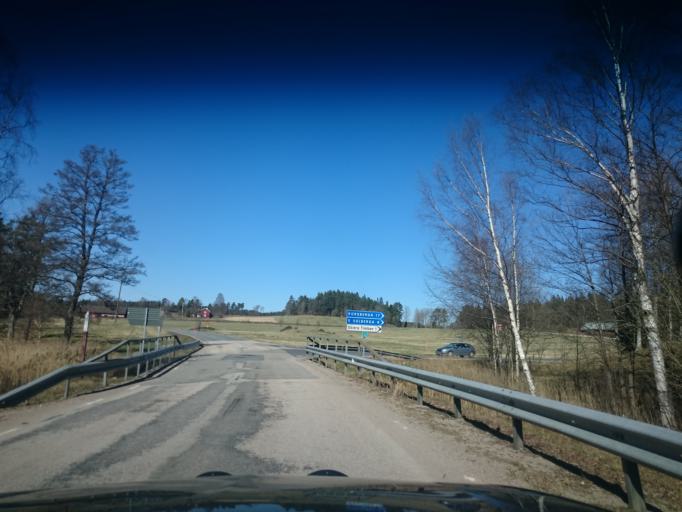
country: SE
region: Joenkoeping
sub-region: Vetlanda Kommun
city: Landsbro
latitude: 57.2187
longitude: 14.9526
